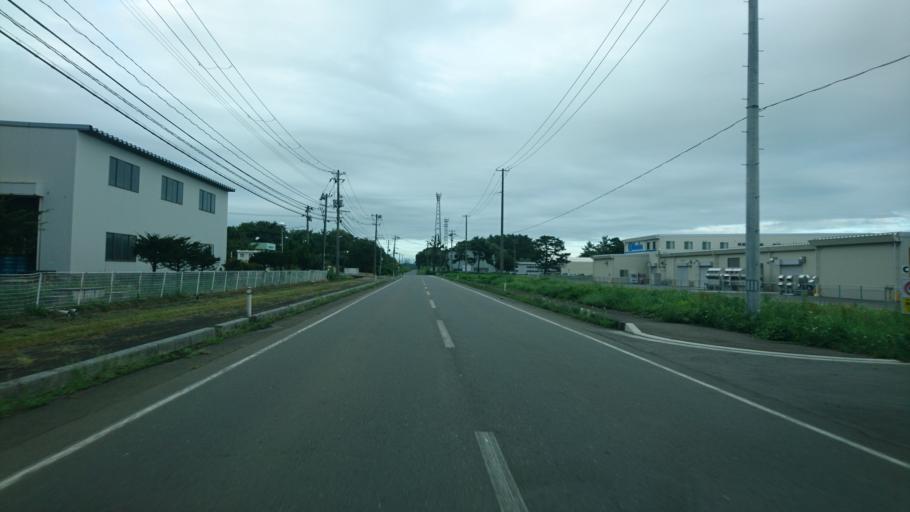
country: JP
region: Iwate
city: Kitakami
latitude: 39.3290
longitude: 141.0101
